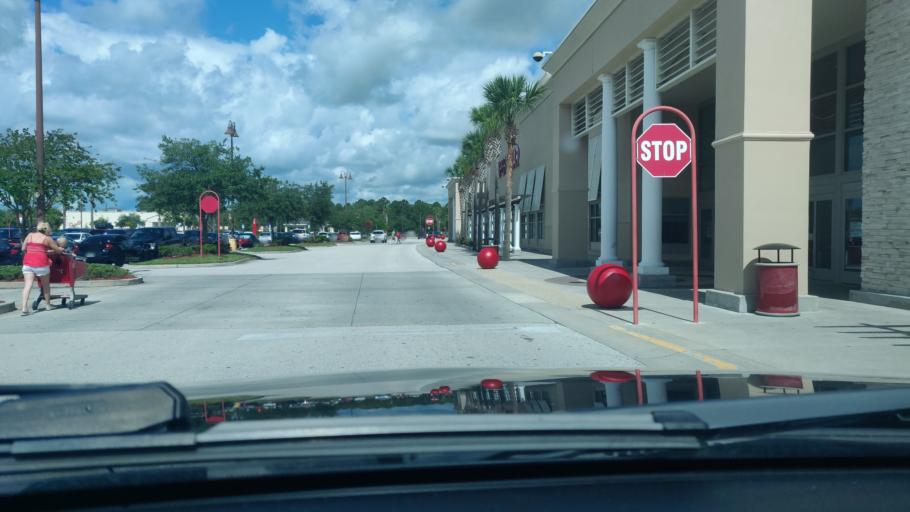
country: US
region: Florida
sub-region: Flagler County
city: Bunnell
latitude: 29.4772
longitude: -81.2183
